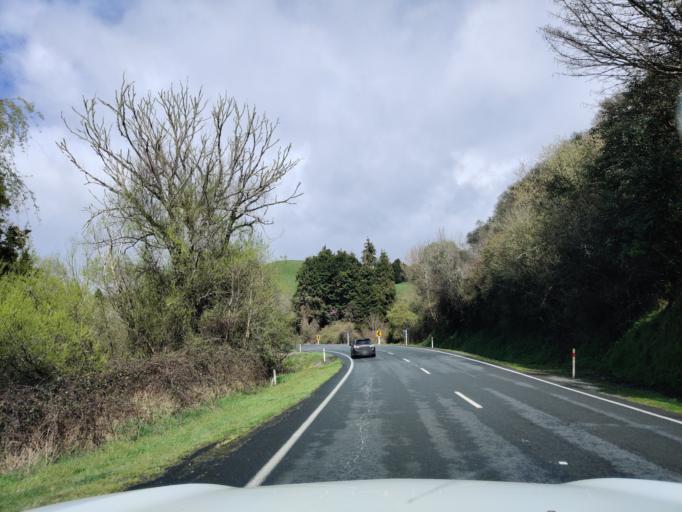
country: NZ
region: Waikato
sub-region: Otorohanga District
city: Otorohanga
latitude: -38.5974
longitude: 175.2180
